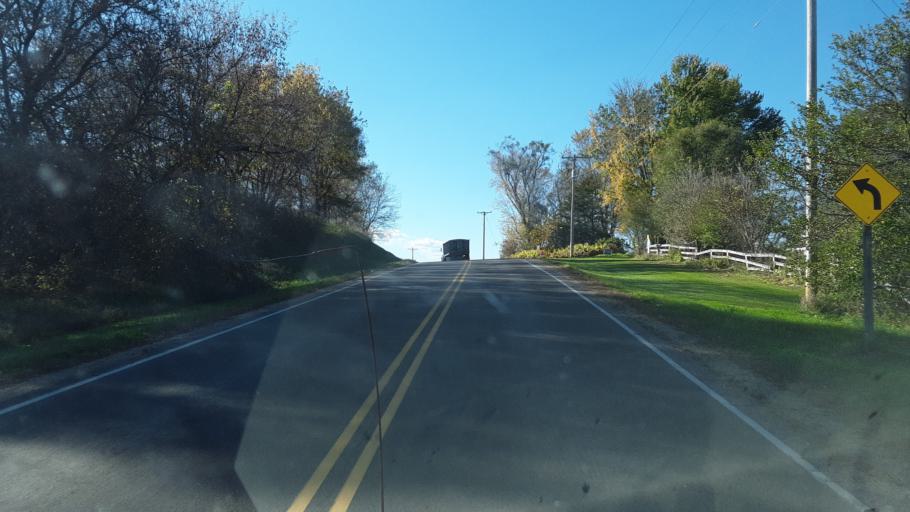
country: US
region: Wisconsin
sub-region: Sauk County
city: Reedsburg
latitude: 43.5408
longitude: -90.1460
